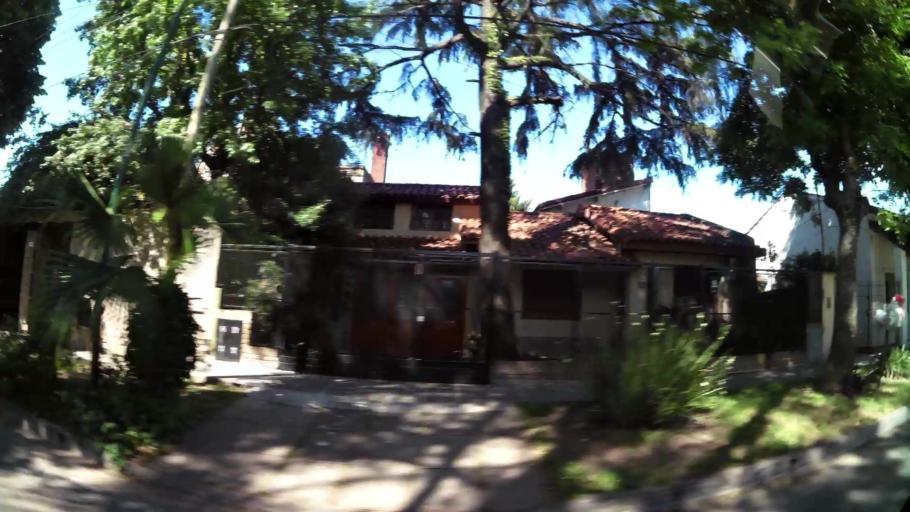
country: AR
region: Buenos Aires
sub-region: Partido de San Isidro
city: San Isidro
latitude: -34.4601
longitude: -58.5378
